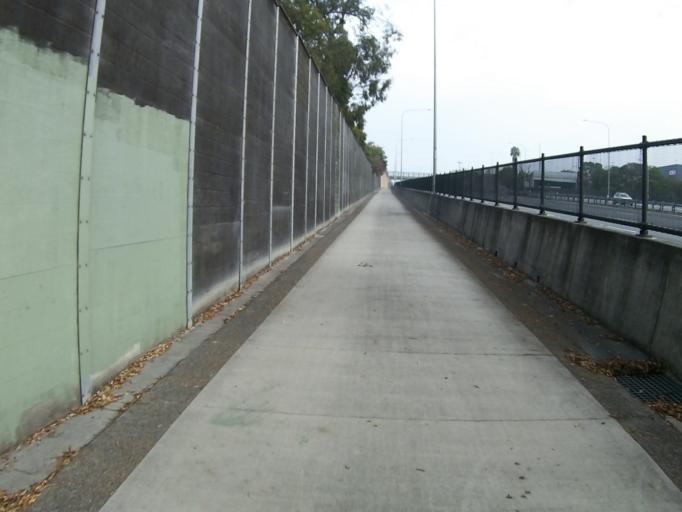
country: AU
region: Queensland
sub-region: Brisbane
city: Upper Mount Gravatt
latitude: -27.5664
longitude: 153.0836
